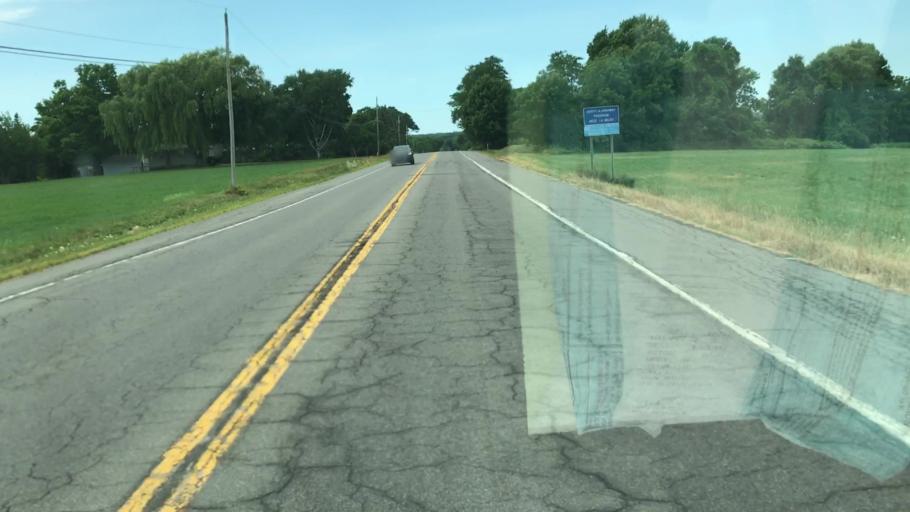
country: US
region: New York
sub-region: Onondaga County
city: Marcellus
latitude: 42.9367
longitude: -76.3682
